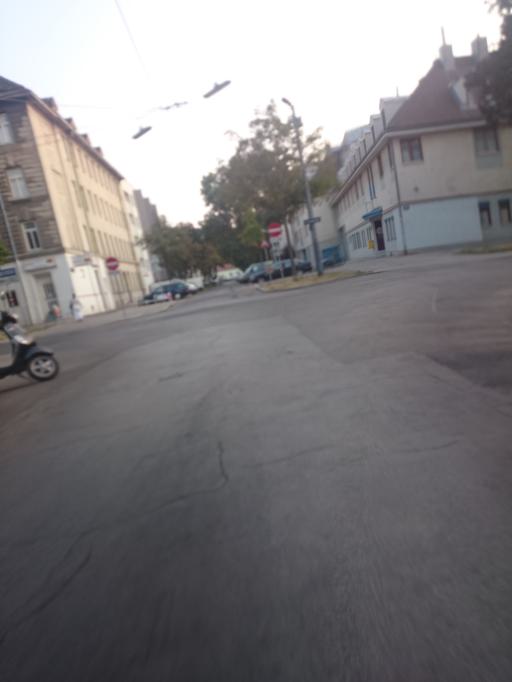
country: AT
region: Vienna
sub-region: Wien Stadt
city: Vienna
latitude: 48.2532
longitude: 16.4071
